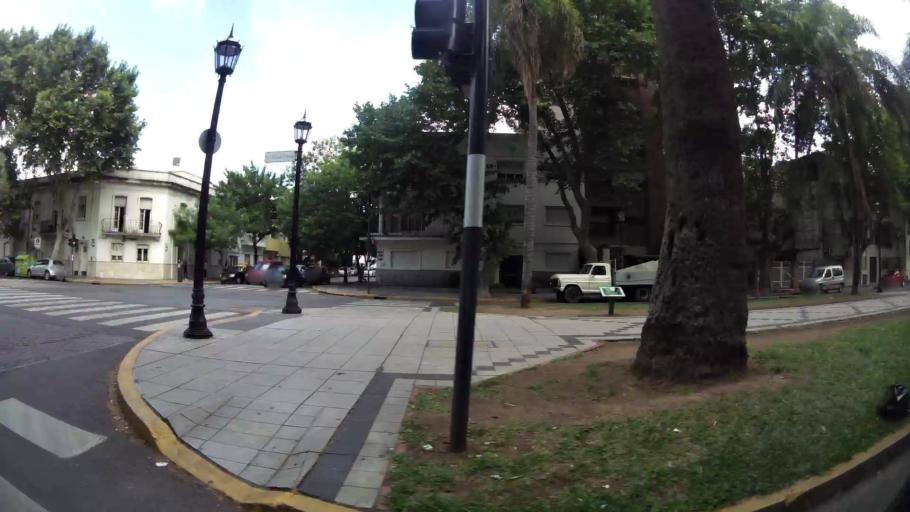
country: AR
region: Santa Fe
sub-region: Departamento de Rosario
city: Rosario
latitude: -32.9343
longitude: -60.6508
